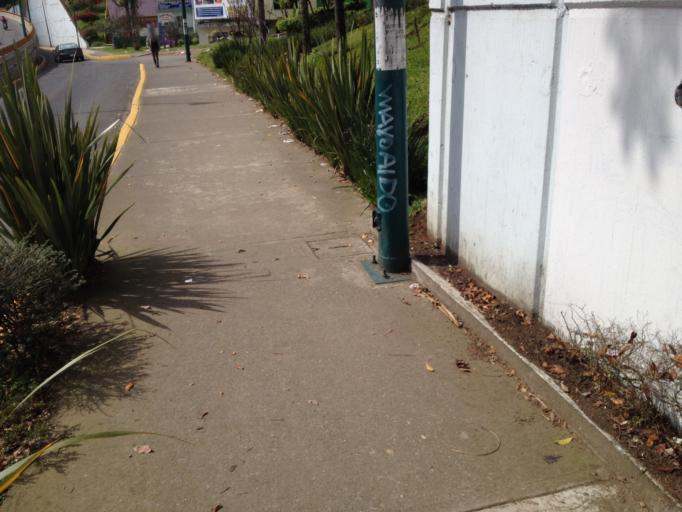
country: MX
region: Veracruz
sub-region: Xalapa
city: Xalapa de Enriquez
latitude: 19.5208
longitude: -96.9134
